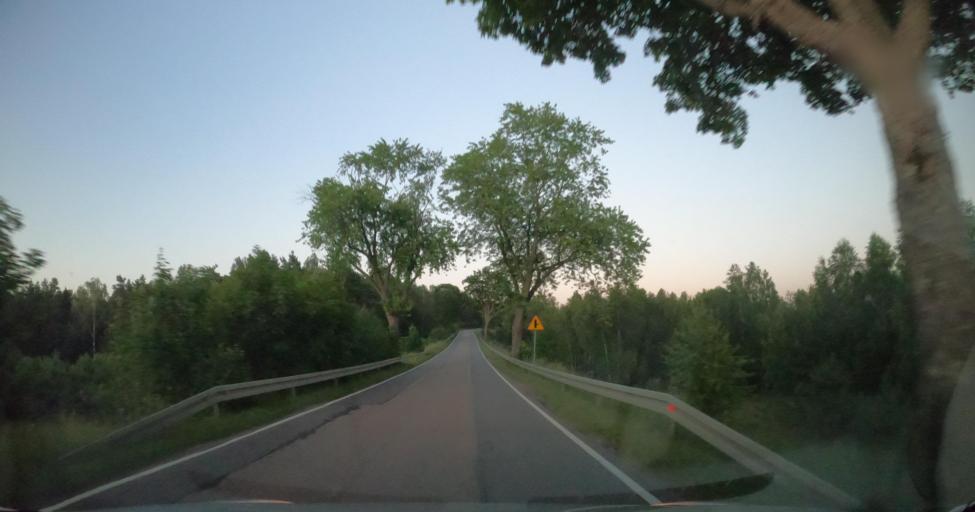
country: PL
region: Pomeranian Voivodeship
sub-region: Powiat wejherowski
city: Luzino
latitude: 54.4647
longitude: 18.1226
